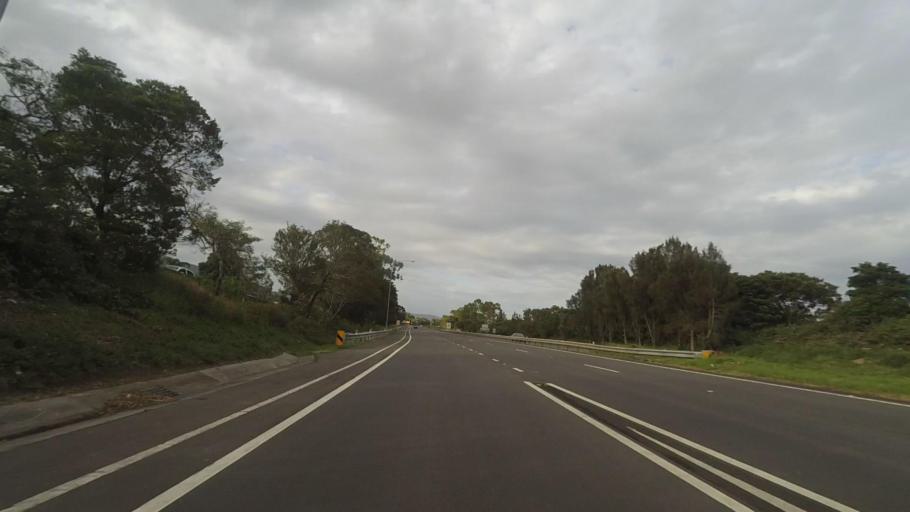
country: AU
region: New South Wales
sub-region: Wollongong
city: Fairy Meadow
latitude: -34.4047
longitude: 150.8924
